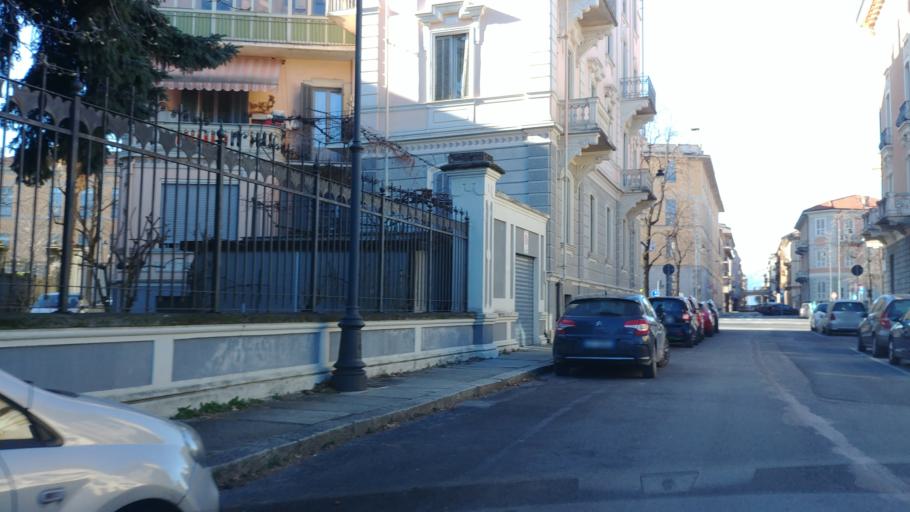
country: IT
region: Piedmont
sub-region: Provincia di Cuneo
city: Cuneo
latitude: 44.3855
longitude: 7.5494
